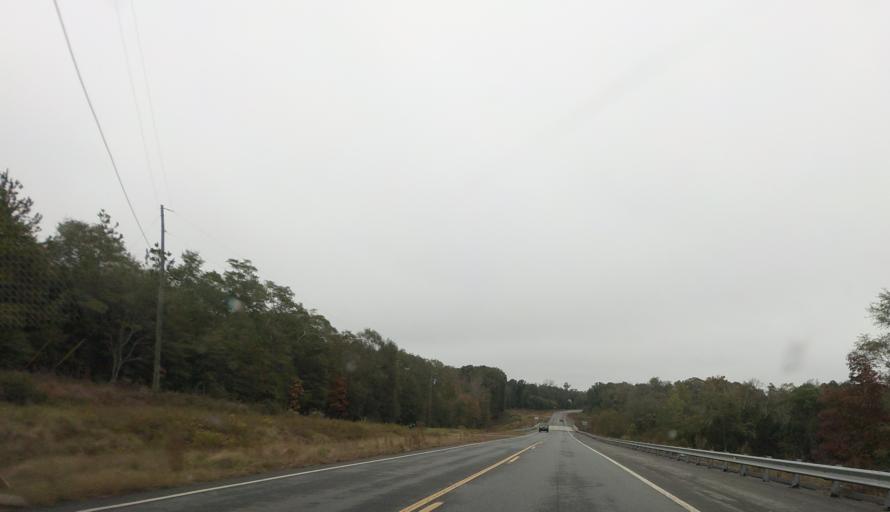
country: US
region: Georgia
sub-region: Marion County
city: Buena Vista
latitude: 32.3770
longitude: -84.4482
